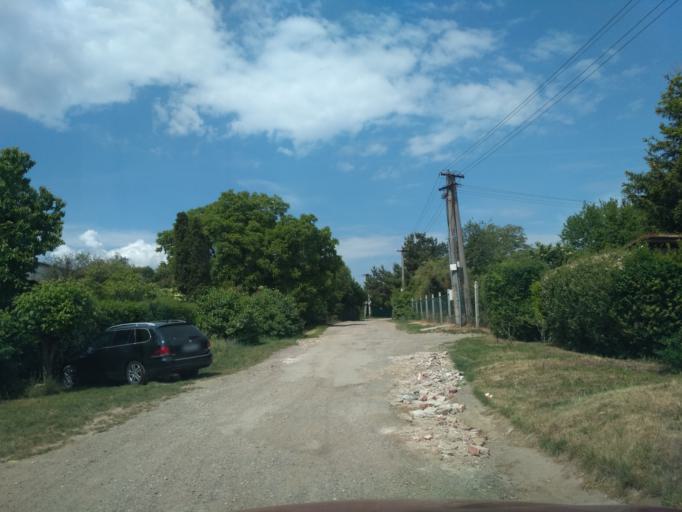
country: SK
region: Kosicky
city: Kosice
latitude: 48.7281
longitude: 21.2261
